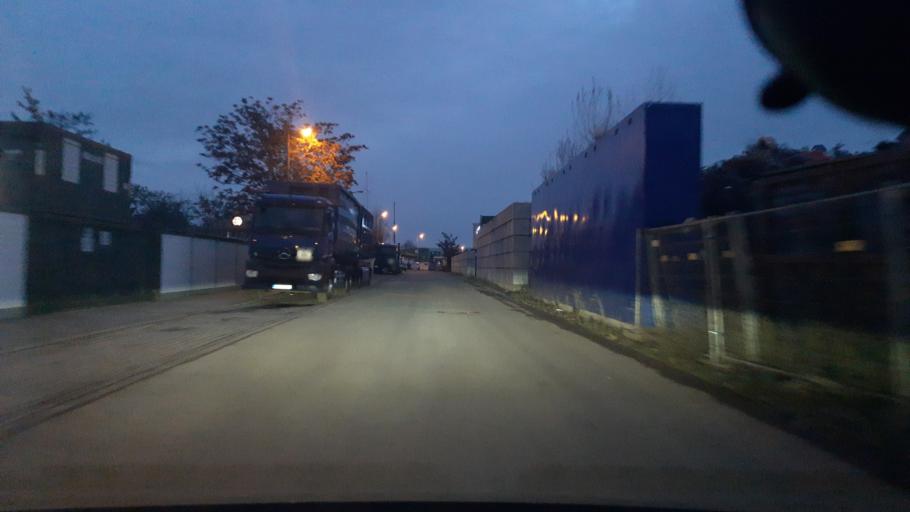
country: DE
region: Rheinland-Pfalz
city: Altrip
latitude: 49.4351
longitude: 8.5191
